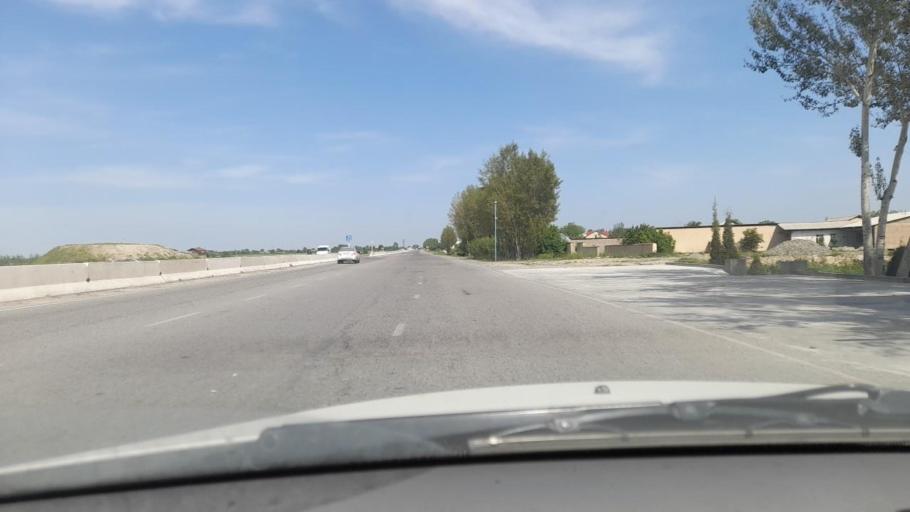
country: UZ
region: Samarqand
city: Kattaqo'rg'on
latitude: 39.9183
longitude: 66.3337
